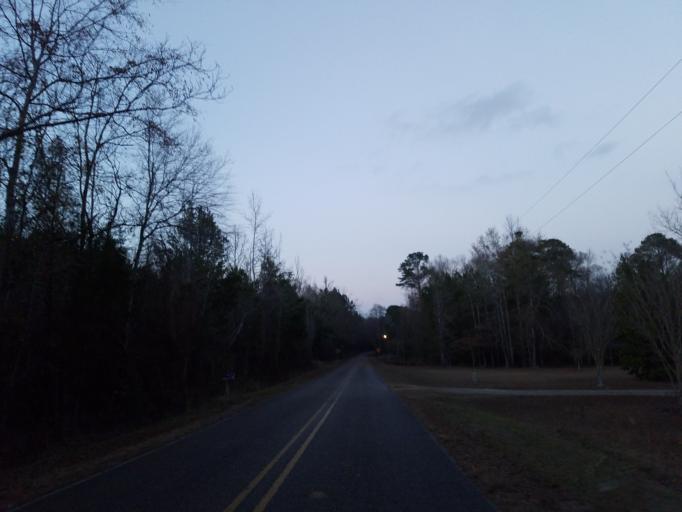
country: US
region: Alabama
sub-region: Sumter County
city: York
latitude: 32.4013
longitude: -88.4599
